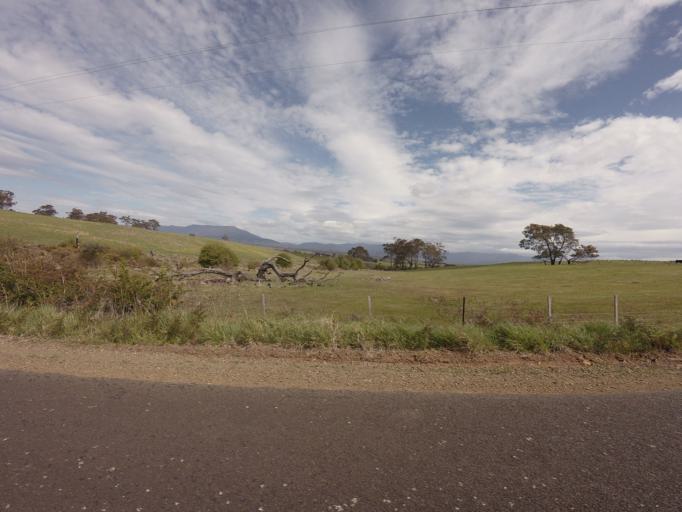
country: AU
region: Tasmania
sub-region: Northern Midlands
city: Longford
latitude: -41.7724
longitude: 147.2212
